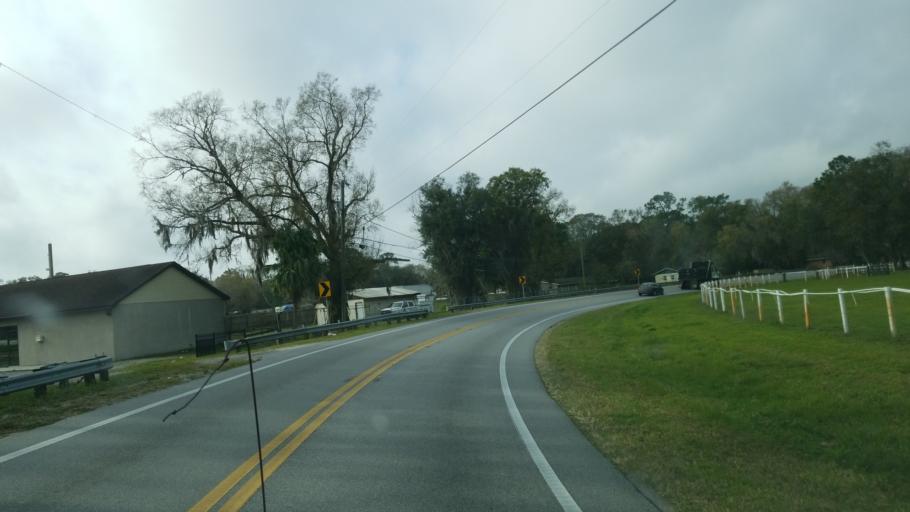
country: US
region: Florida
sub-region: Polk County
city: Winston
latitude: 28.0592
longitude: -82.0065
